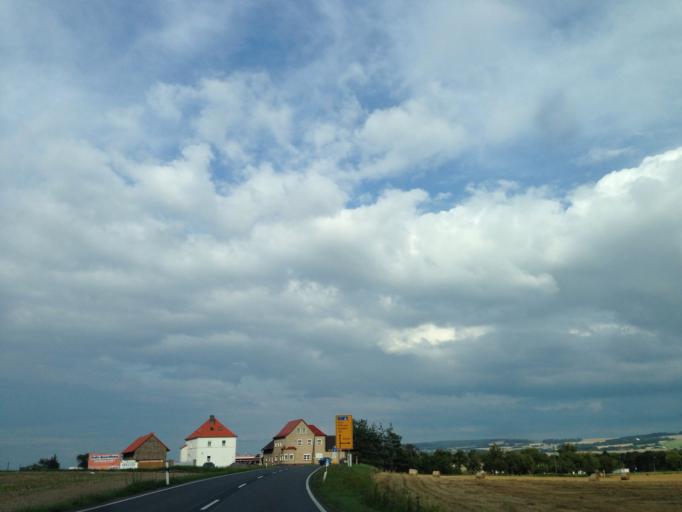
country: DE
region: Thuringia
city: Konitz
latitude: 50.6643
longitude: 11.4899
